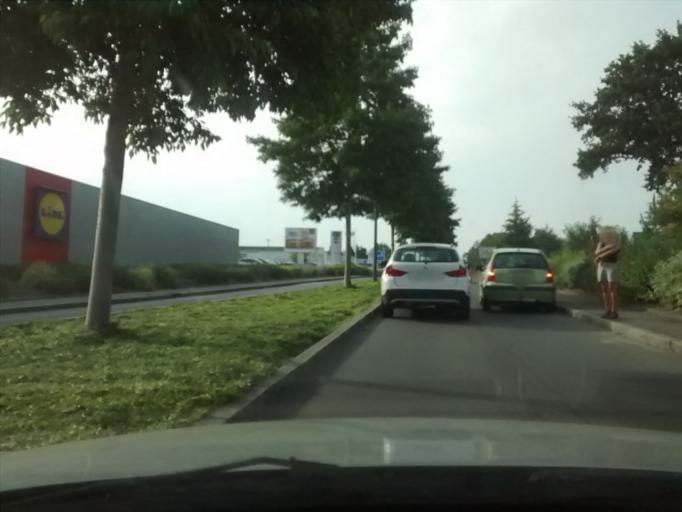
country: FR
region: Brittany
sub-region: Departement d'Ille-et-Vilaine
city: Vitre
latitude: 48.1071
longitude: -1.2076
